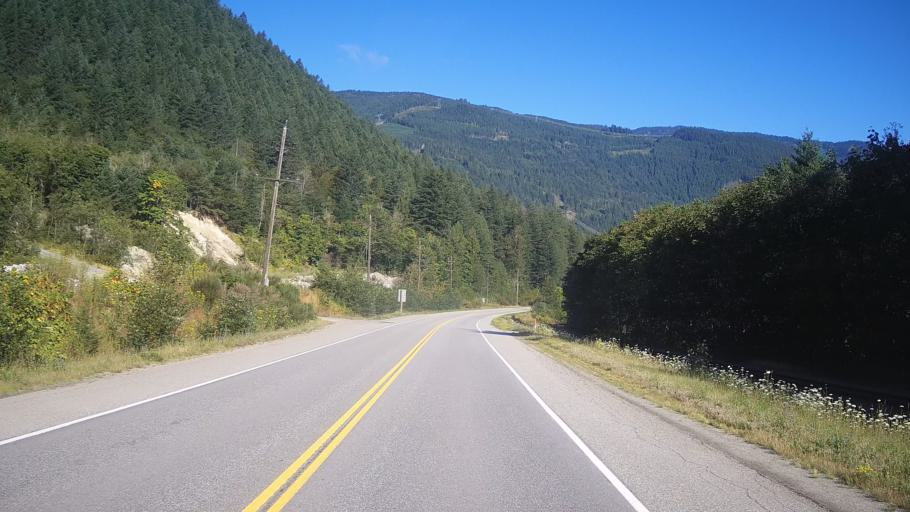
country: CA
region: British Columbia
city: Hope
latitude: 49.5391
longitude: -121.4334
